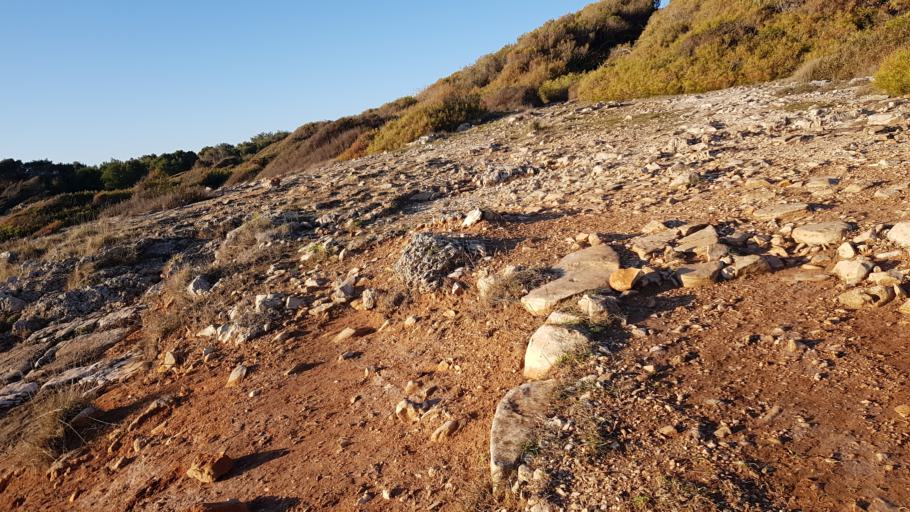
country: IT
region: Apulia
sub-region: Provincia di Lecce
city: Nardo
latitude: 40.1483
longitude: 17.9712
